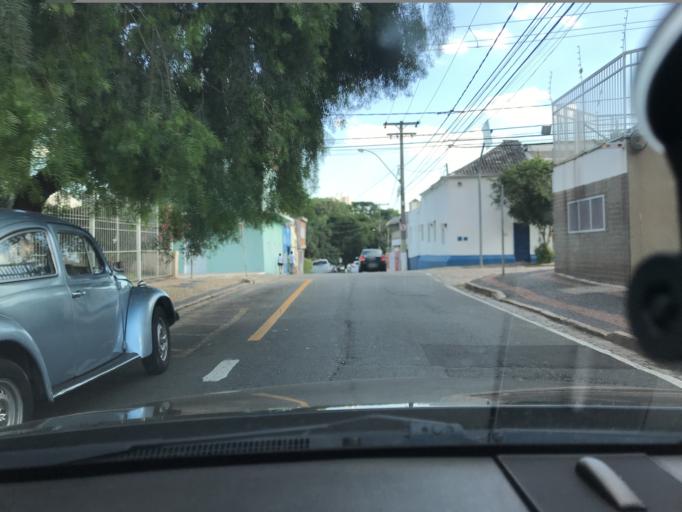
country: BR
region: Sao Paulo
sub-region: Campinas
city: Campinas
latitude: -22.9070
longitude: -47.0517
